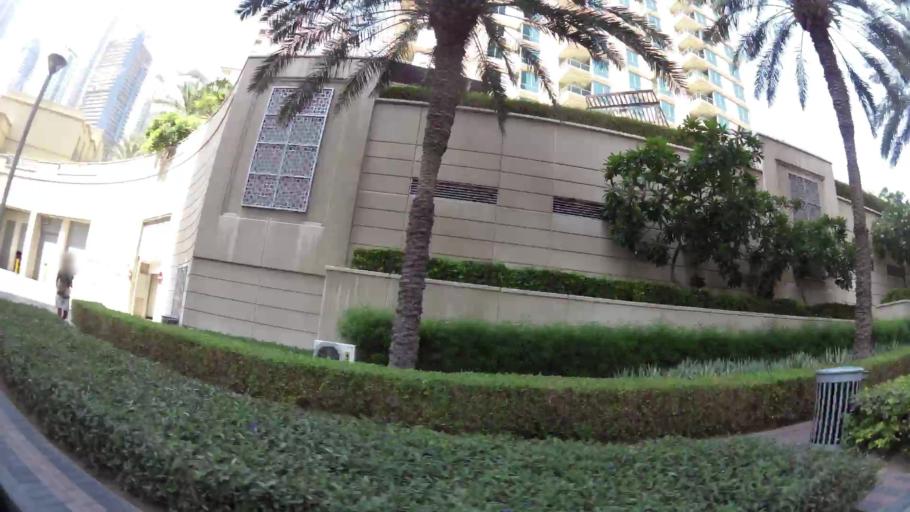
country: AE
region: Dubai
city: Dubai
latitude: 25.0833
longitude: 55.1481
